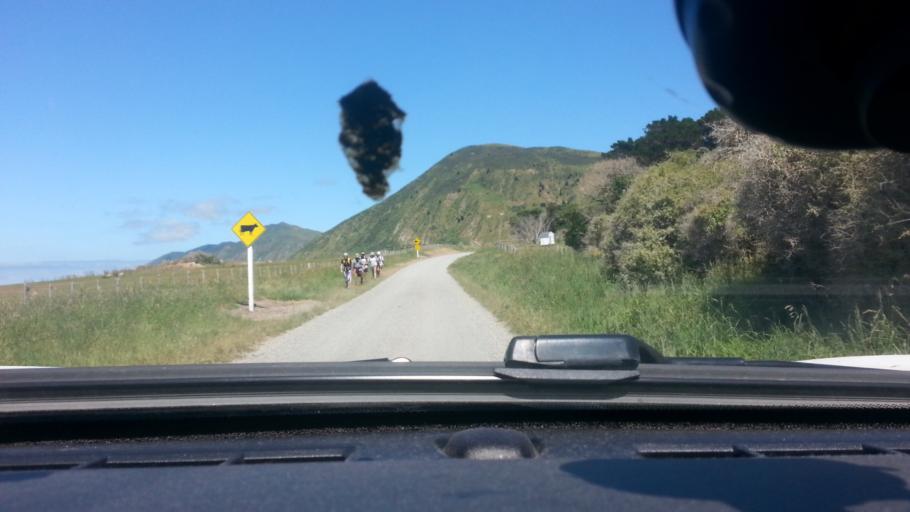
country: NZ
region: Wellington
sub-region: South Wairarapa District
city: Waipawa
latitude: -41.4946
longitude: 175.5476
